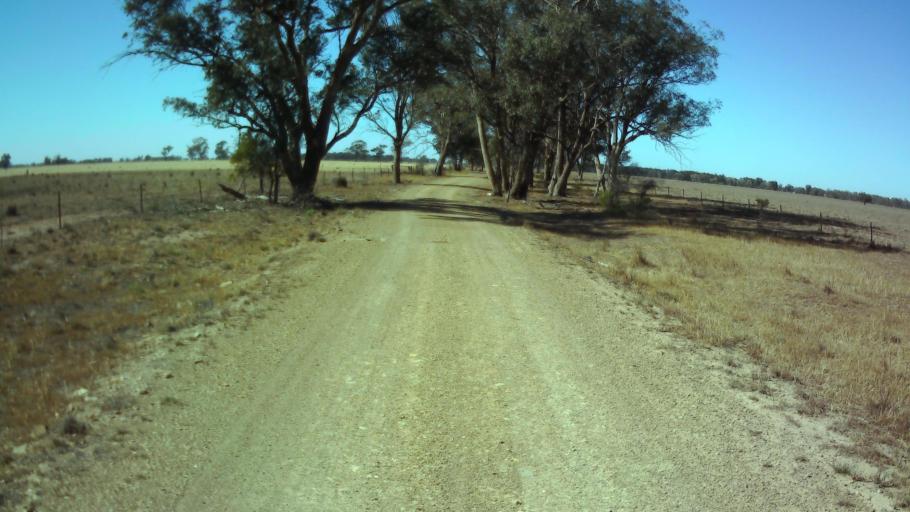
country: AU
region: New South Wales
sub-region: Weddin
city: Grenfell
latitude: -33.9456
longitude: 147.8701
